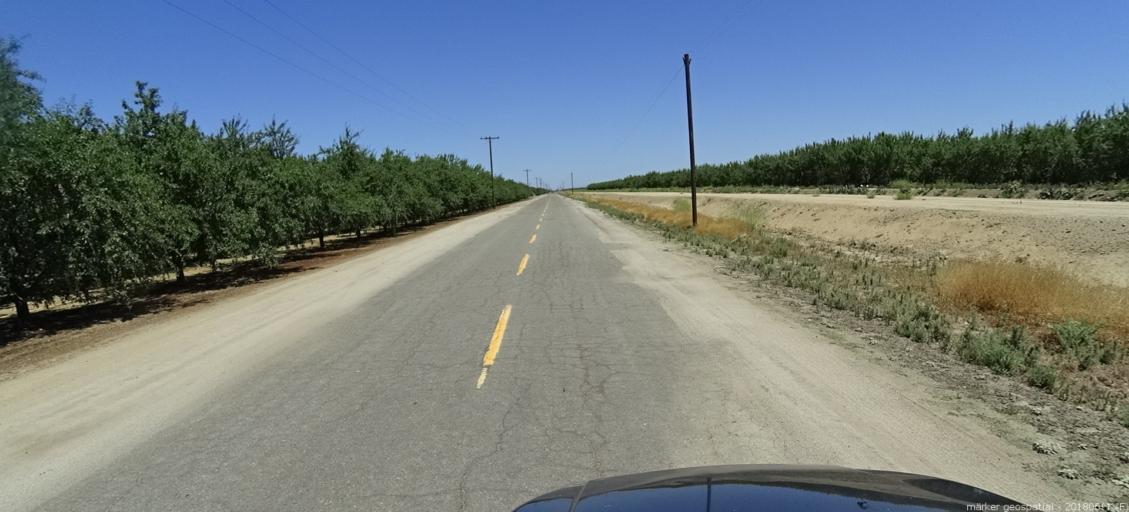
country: US
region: California
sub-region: Madera County
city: Fairmead
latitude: 37.0340
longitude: -120.2205
